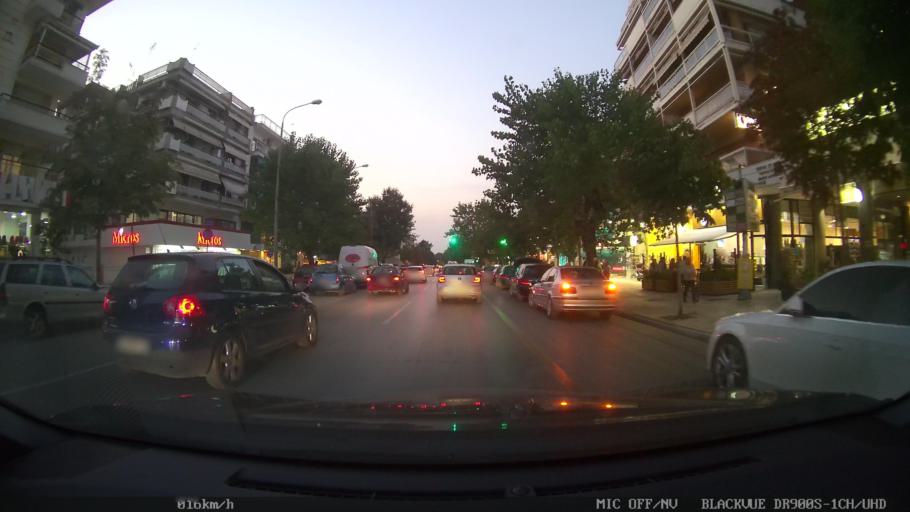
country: GR
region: Central Macedonia
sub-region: Nomos Thessalonikis
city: Kalamaria
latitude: 40.5887
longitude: 22.9606
